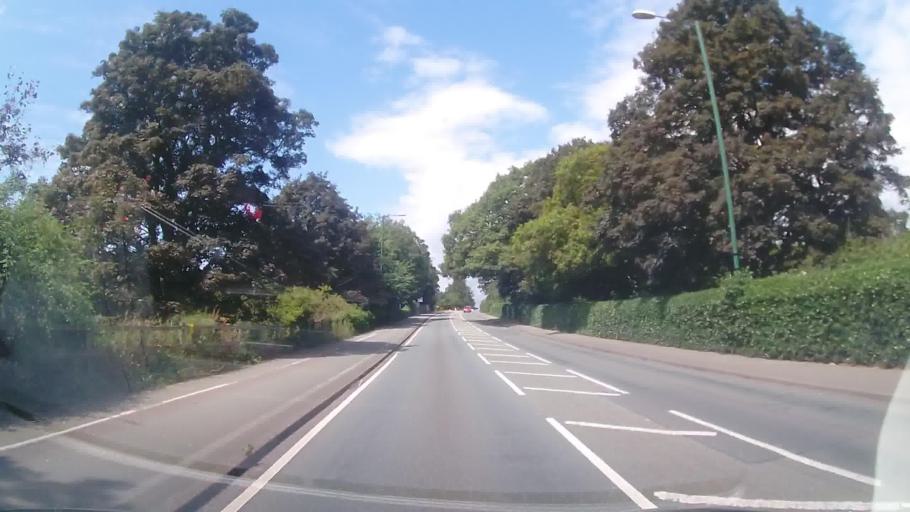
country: GB
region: England
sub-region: Shropshire
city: Shrewsbury
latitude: 52.6958
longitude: -2.7619
